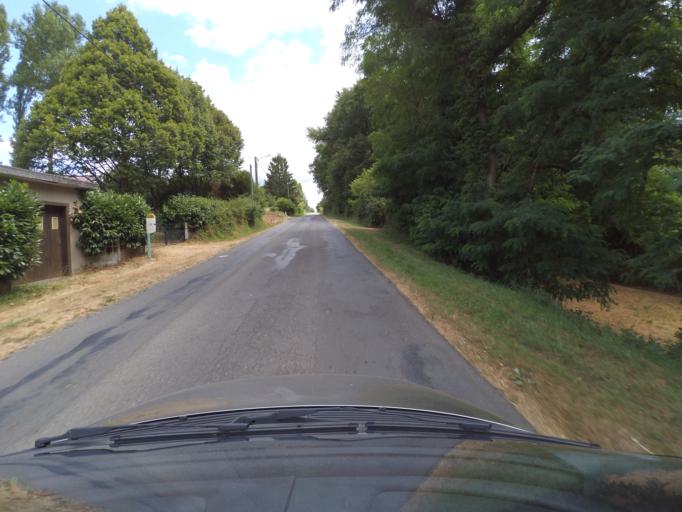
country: FR
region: Centre
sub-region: Departement de l'Indre
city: Belabre
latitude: 46.4656
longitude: 1.0481
